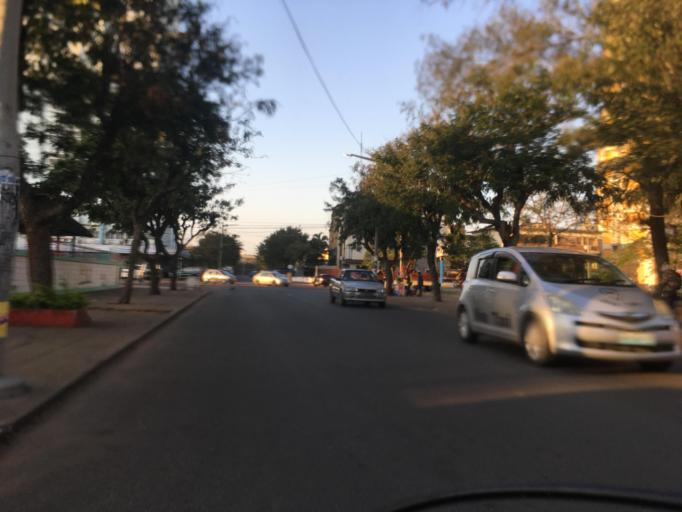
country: MZ
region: Maputo City
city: Maputo
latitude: -25.9668
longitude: 32.5942
